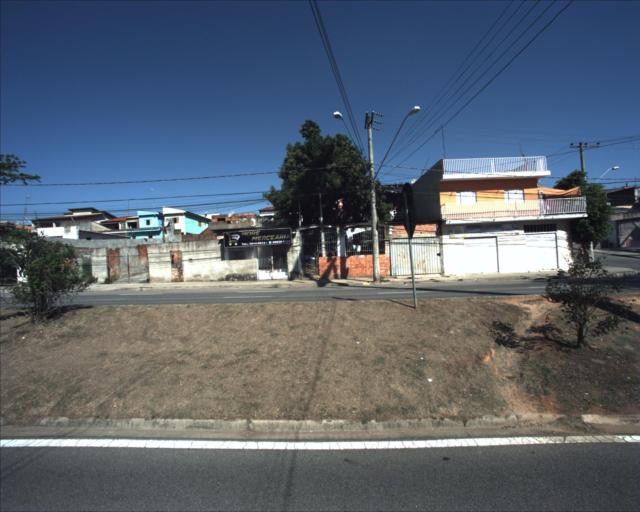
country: BR
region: Sao Paulo
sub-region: Sorocaba
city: Sorocaba
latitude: -23.4539
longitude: -47.4728
